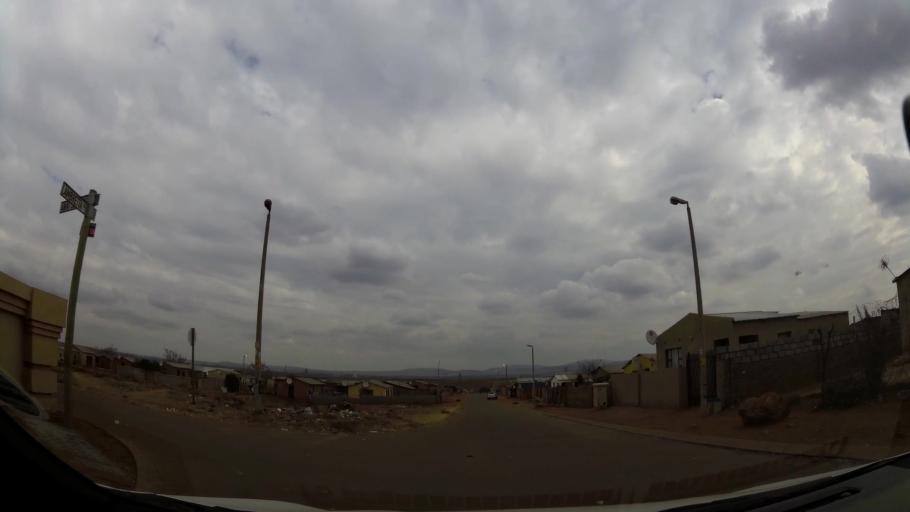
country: ZA
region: Gauteng
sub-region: Ekurhuleni Metropolitan Municipality
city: Germiston
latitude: -26.3843
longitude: 28.1204
